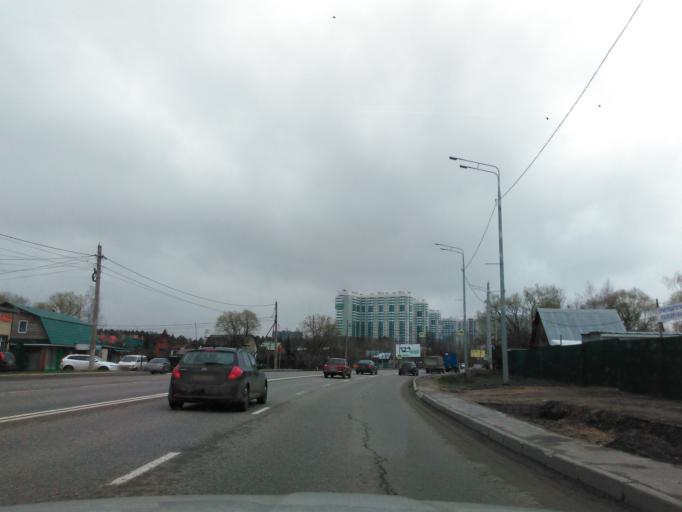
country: RU
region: Moskovskaya
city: Opalikha
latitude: 55.8389
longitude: 37.2551
